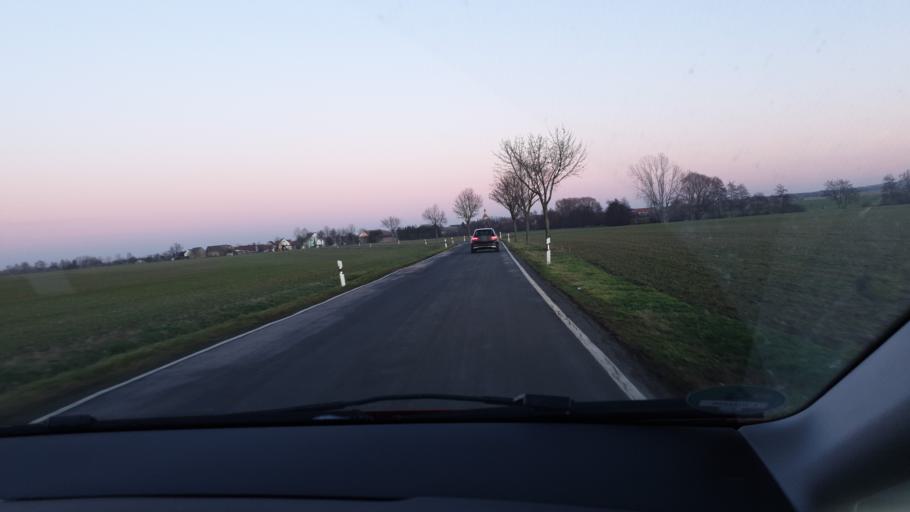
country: DE
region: Saxony
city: Mockrehna
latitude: 51.4687
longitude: 12.7962
